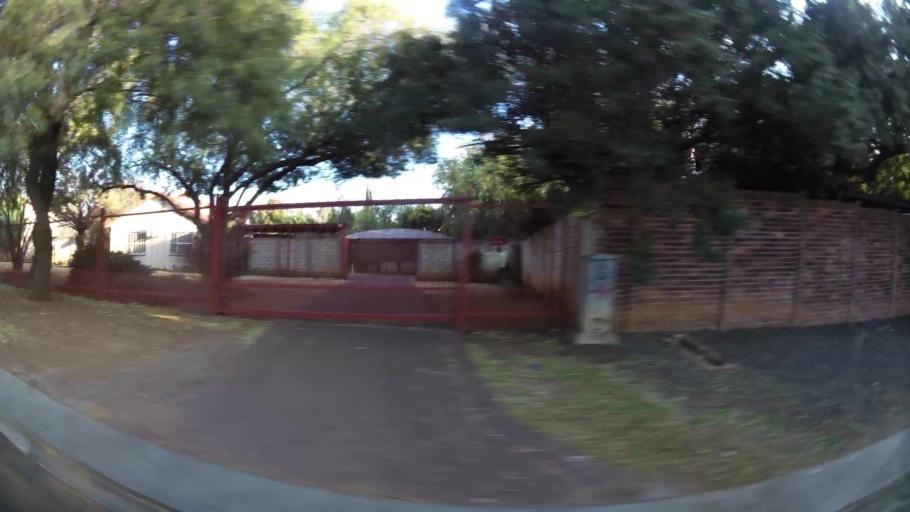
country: ZA
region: Orange Free State
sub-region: Mangaung Metropolitan Municipality
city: Bloemfontein
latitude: -29.1465
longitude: 26.1635
